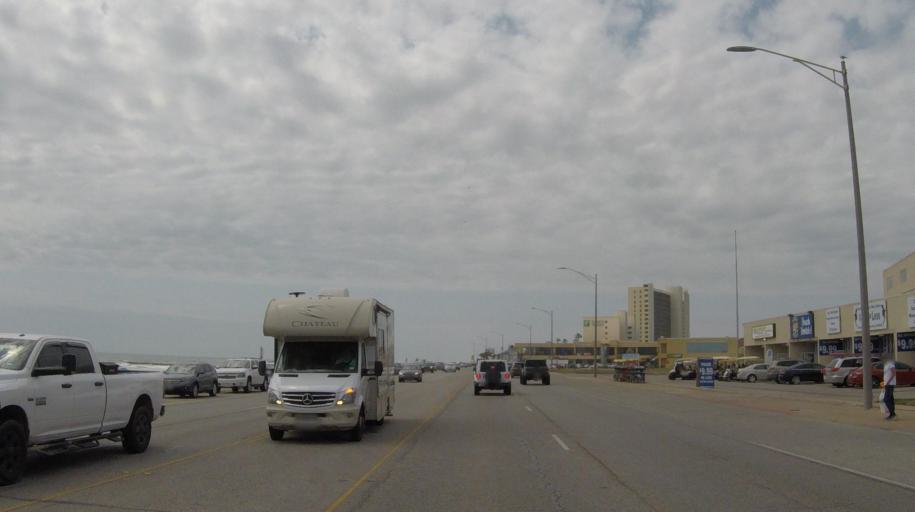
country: US
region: Texas
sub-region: Galveston County
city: Galveston
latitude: 29.2745
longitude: -94.8128
